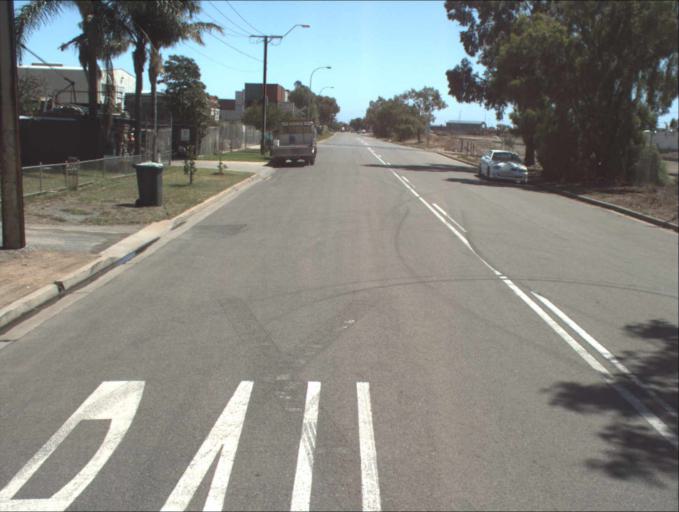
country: AU
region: South Australia
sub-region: Charles Sturt
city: Woodville North
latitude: -34.8402
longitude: 138.5500
